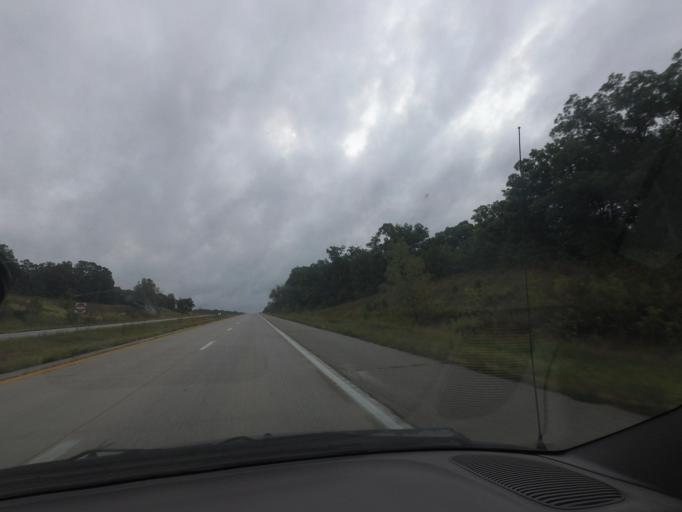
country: US
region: Missouri
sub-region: Shelby County
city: Shelbina
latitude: 39.6696
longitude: -91.9000
